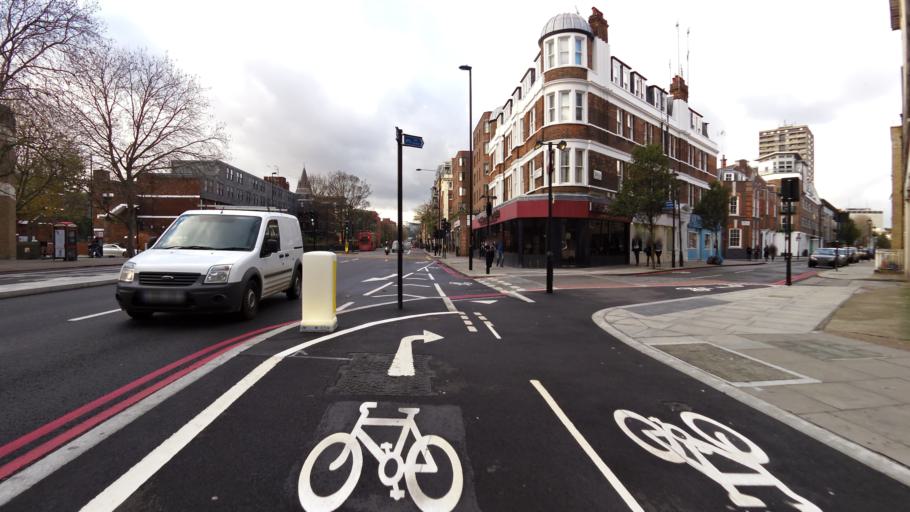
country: GB
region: England
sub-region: Greater London
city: City of Westminster
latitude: 51.4899
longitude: -0.1321
